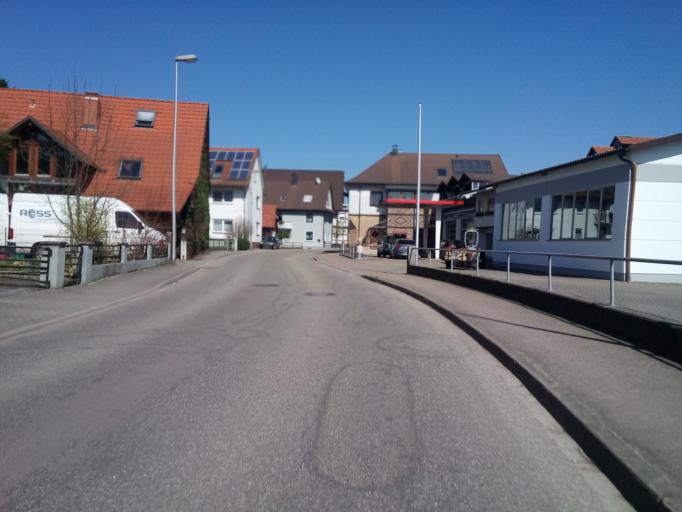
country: FR
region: Alsace
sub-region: Departement du Bas-Rhin
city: La Wantzenau
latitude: 48.6235
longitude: 7.8543
